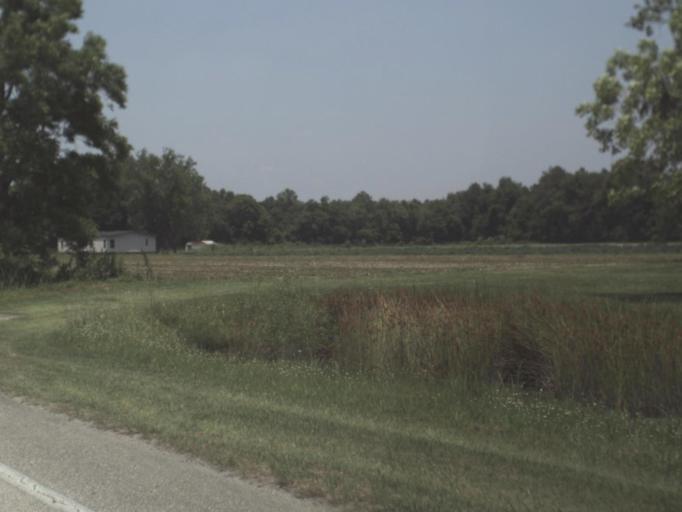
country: US
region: Florida
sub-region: Bradford County
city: Starke
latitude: 30.0641
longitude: -82.0660
